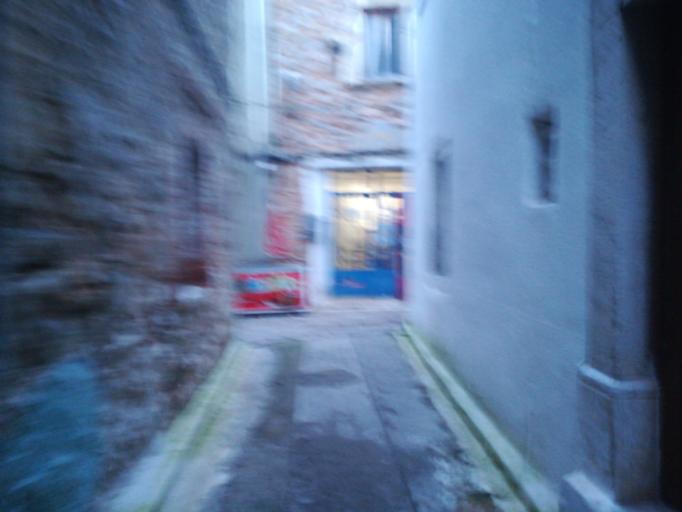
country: GR
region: North Aegean
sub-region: Chios
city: Thymiana
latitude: 38.2473
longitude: 25.9420
